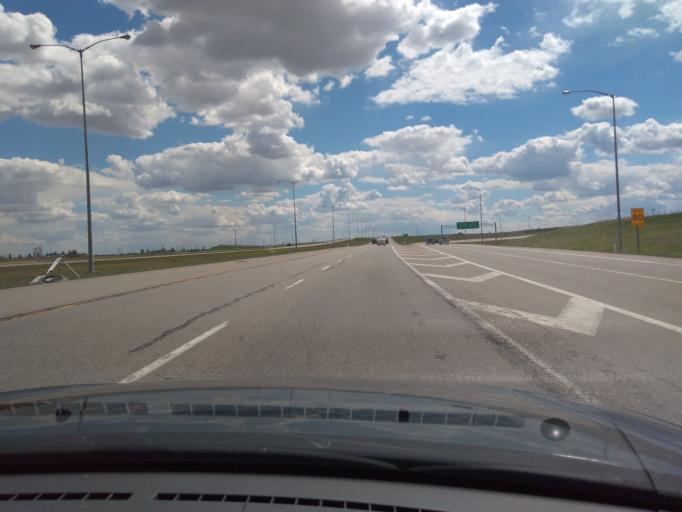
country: CA
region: Alberta
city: Chestermere
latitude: 51.0744
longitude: -113.9207
